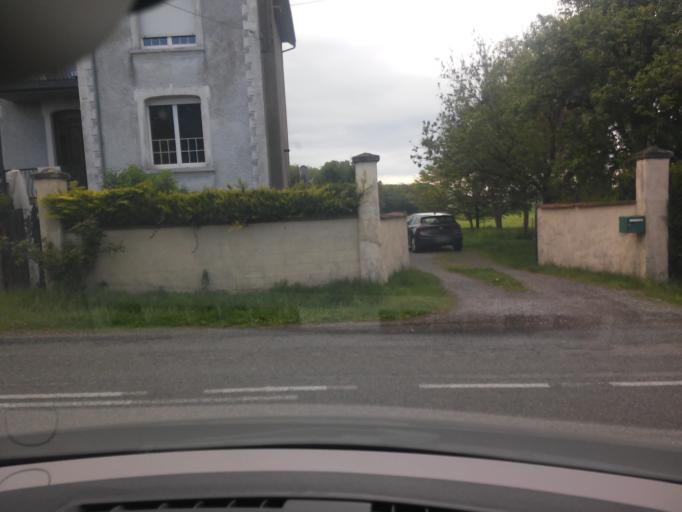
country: FR
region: Lorraine
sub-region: Departement de Meurthe-et-Moselle
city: Longuyon
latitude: 49.3152
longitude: 5.4913
